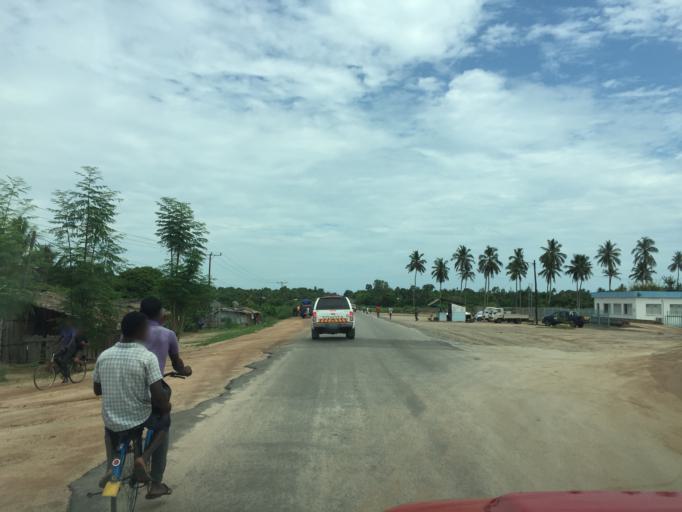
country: MZ
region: Zambezia
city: Quelimane
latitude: -17.5914
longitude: 36.8131
